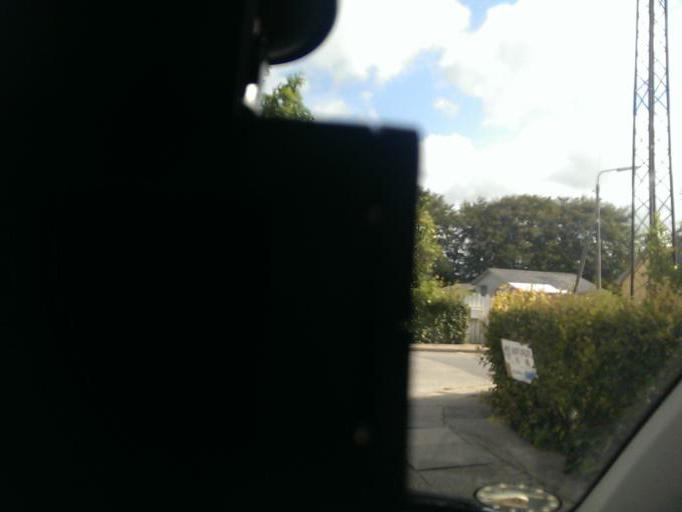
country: DK
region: North Denmark
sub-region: Hjorring Kommune
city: Vra
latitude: 57.3513
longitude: 9.9401
